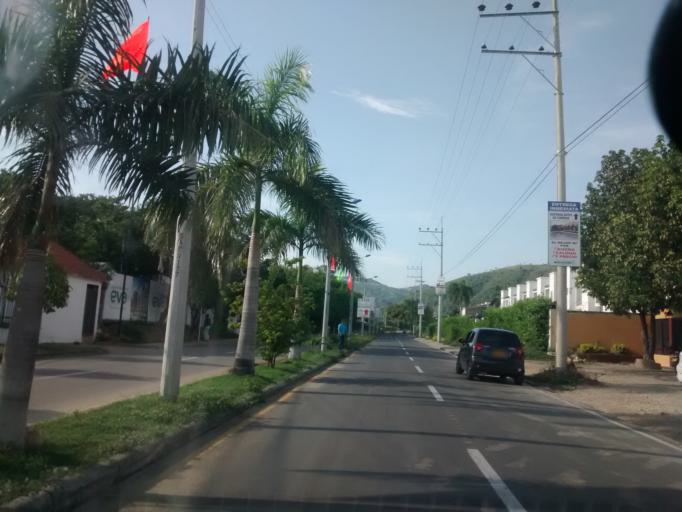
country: CO
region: Cundinamarca
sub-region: Girardot
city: Girardot City
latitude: 4.3087
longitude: -74.8148
